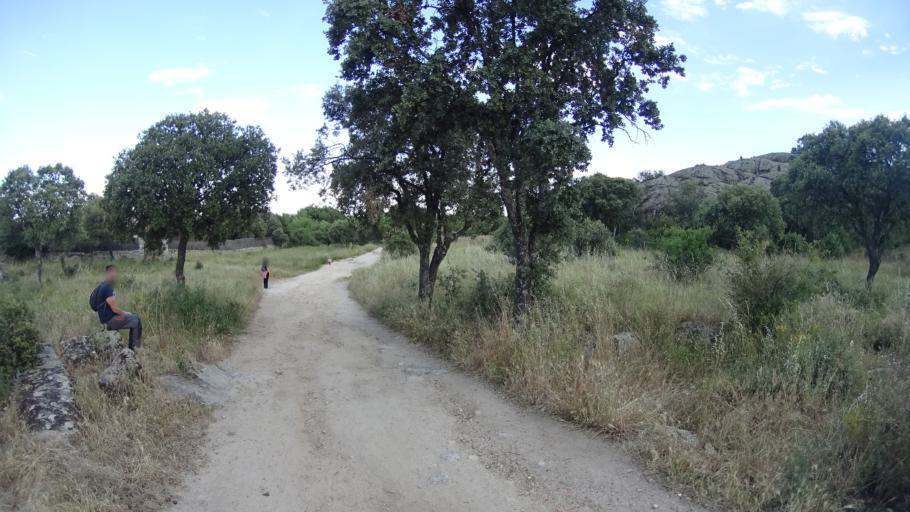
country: ES
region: Madrid
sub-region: Provincia de Madrid
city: Hoyo de Manzanares
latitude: 40.6264
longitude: -3.9159
